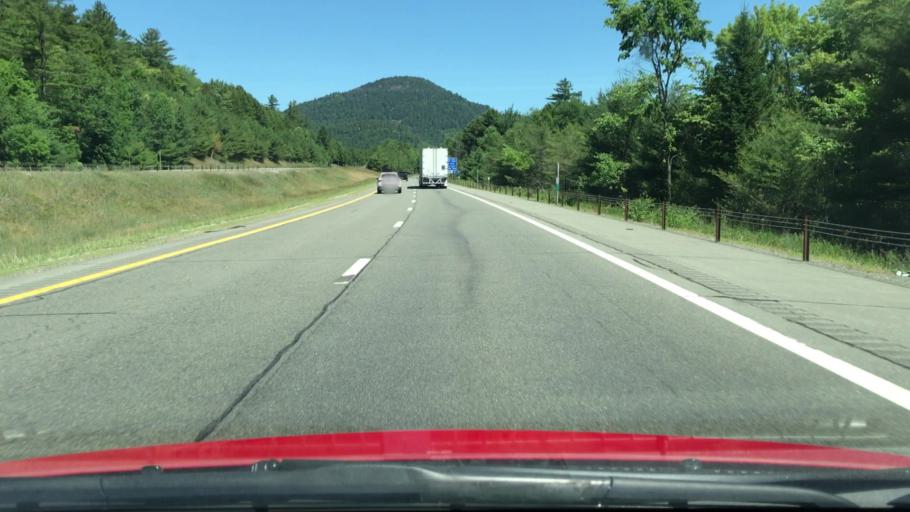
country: US
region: New York
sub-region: Essex County
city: Mineville
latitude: 43.9830
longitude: -73.7230
